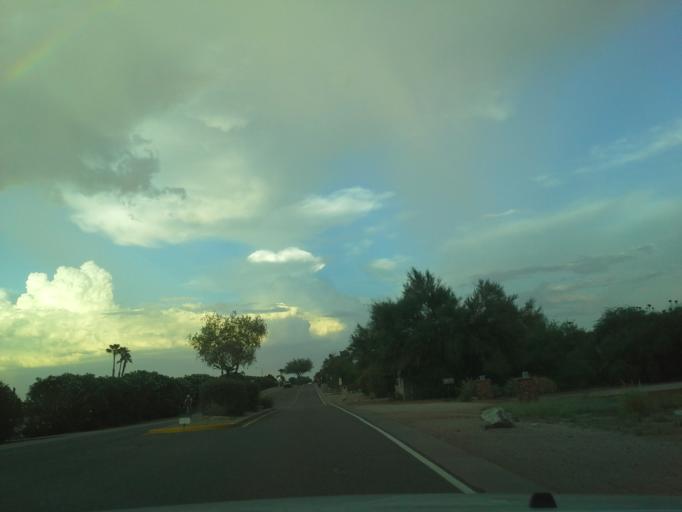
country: US
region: Arizona
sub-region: Maricopa County
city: Paradise Valley
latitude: 33.5238
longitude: -111.9649
